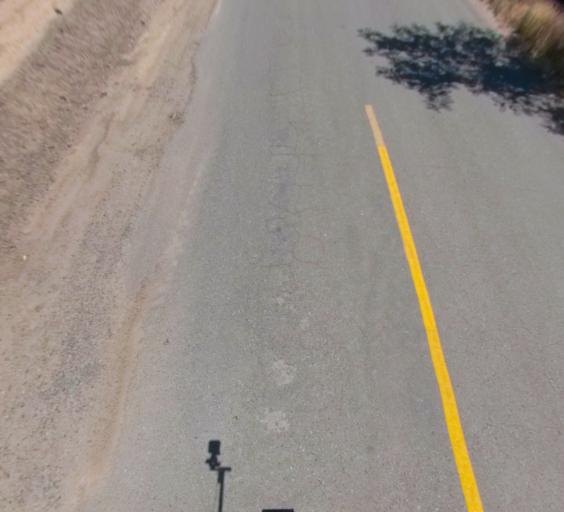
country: US
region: California
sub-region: Fresno County
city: Fresno
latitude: 36.8592
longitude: -119.8214
